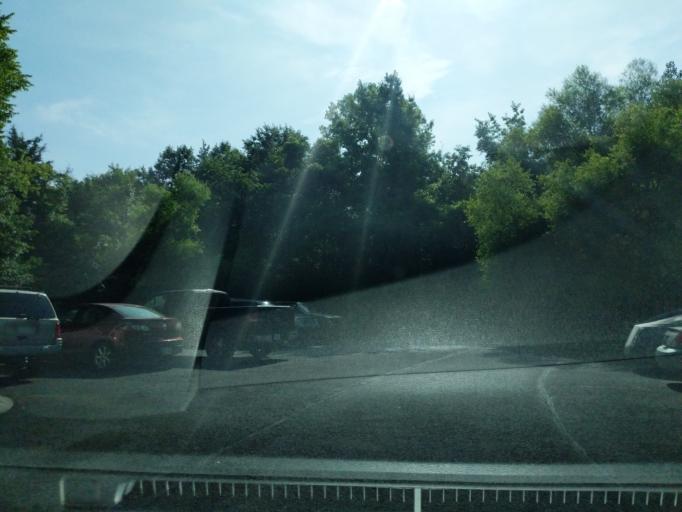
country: US
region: Tennessee
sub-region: Sumner County
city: Hendersonville
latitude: 36.3117
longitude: -86.6532
